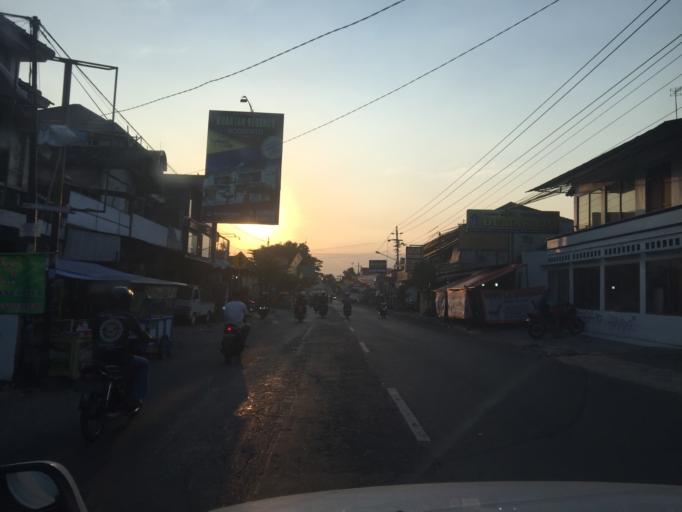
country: ID
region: Daerah Istimewa Yogyakarta
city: Gamping Lor
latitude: -7.7779
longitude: 110.3348
